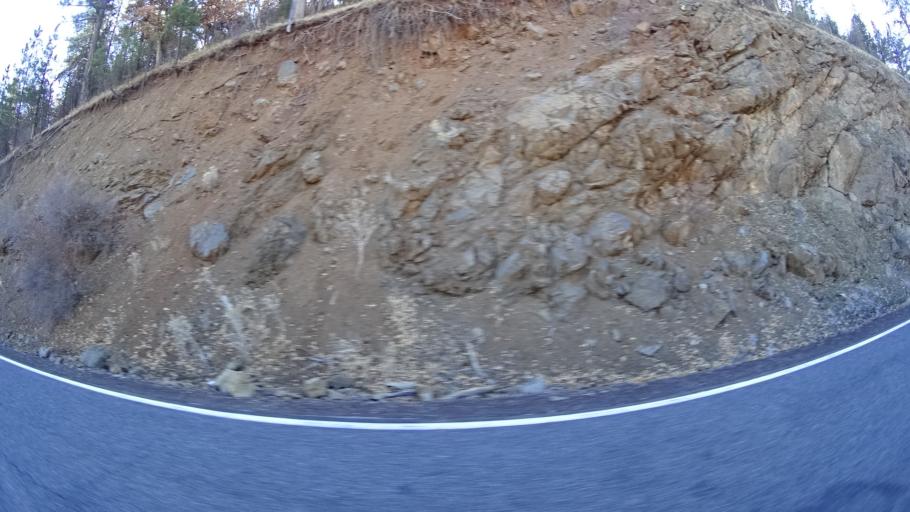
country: US
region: California
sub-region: Siskiyou County
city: Weed
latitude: 41.4721
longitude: -122.5853
